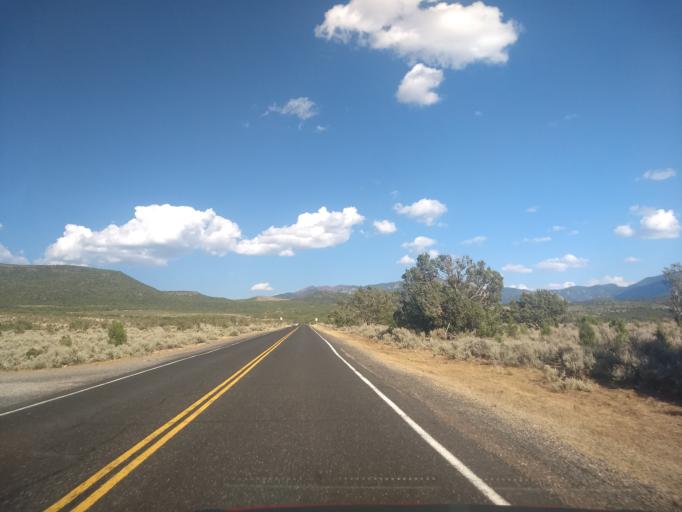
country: US
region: Utah
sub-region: Washington County
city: Enterprise
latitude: 37.4185
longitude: -113.5573
